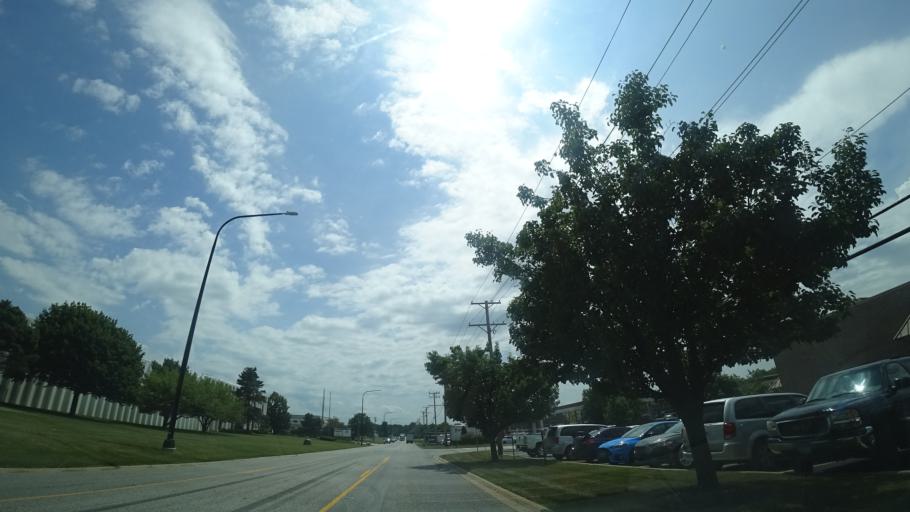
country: US
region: Illinois
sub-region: Cook County
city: Crestwood
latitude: 41.6756
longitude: -87.7586
